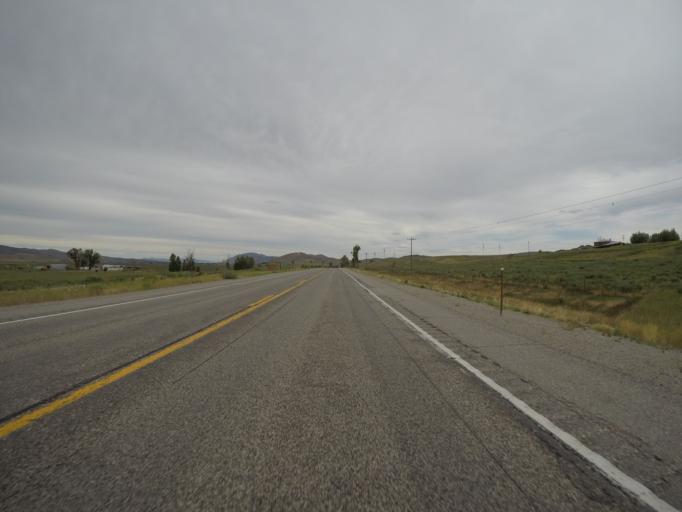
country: US
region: Utah
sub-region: Rich County
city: Randolph
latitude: 42.0466
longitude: -110.9313
